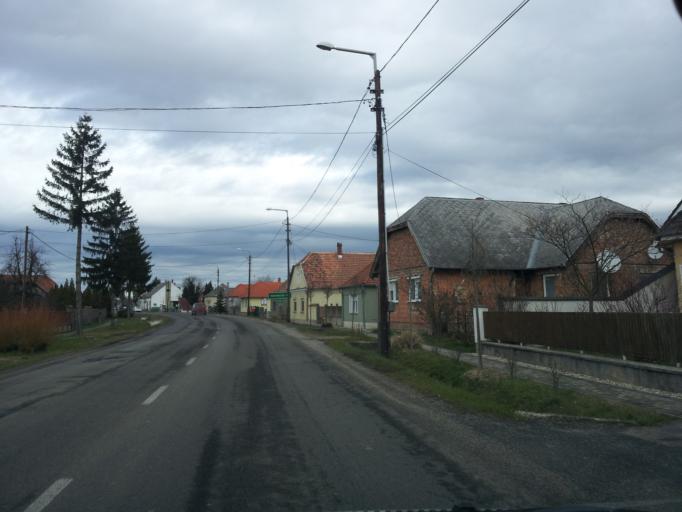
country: HU
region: Vas
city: Gencsapati
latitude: 47.3383
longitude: 16.5806
